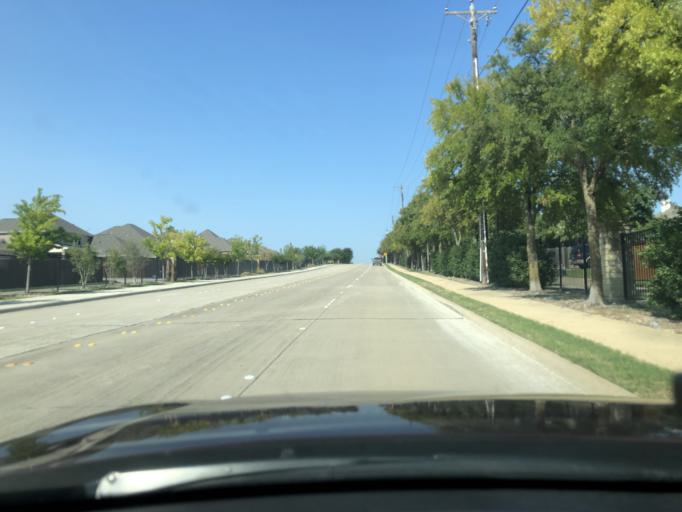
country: US
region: Texas
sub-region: Rockwall County
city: Rockwall
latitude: 32.9411
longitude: -96.4648
